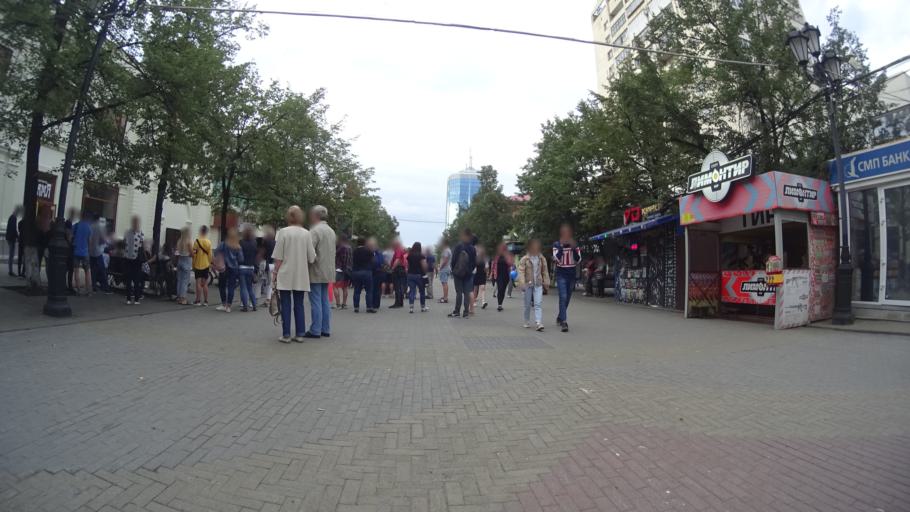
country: RU
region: Chelyabinsk
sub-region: Gorod Chelyabinsk
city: Chelyabinsk
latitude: 55.1613
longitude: 61.4007
